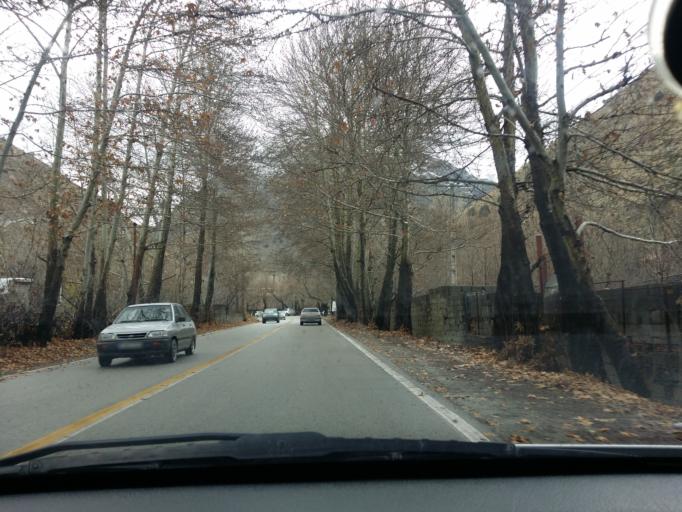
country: IR
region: Tehran
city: Tajrish
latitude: 36.0275
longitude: 51.2435
